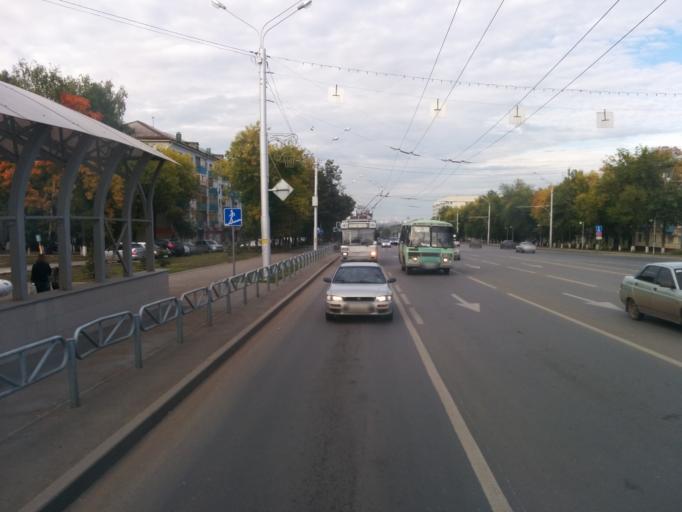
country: RU
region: Bashkortostan
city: Ufa
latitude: 54.7903
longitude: 56.0360
